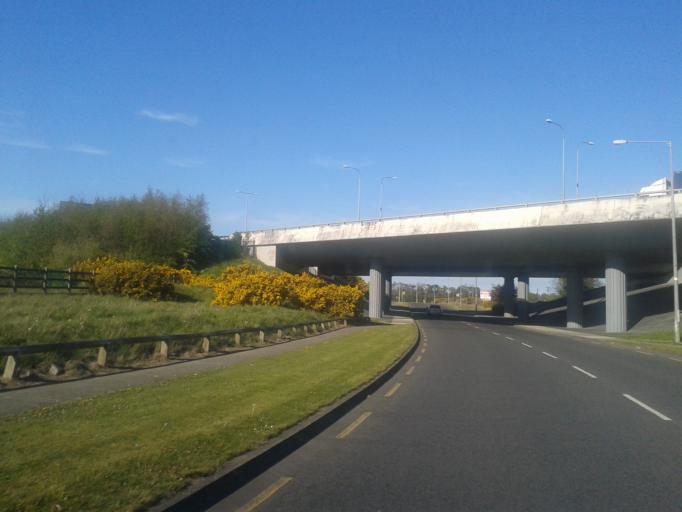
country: IE
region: Leinster
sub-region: Fingal County
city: Swords
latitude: 53.4613
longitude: -6.2050
